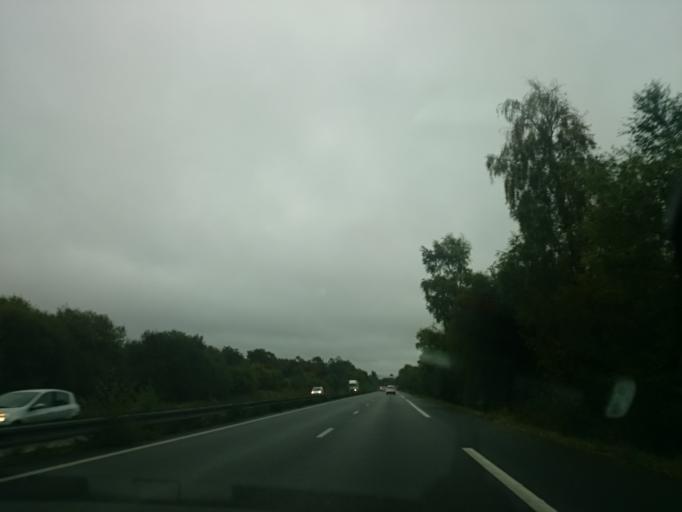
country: FR
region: Brittany
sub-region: Departement du Morbihan
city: Landevant
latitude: 47.7661
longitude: -3.1560
